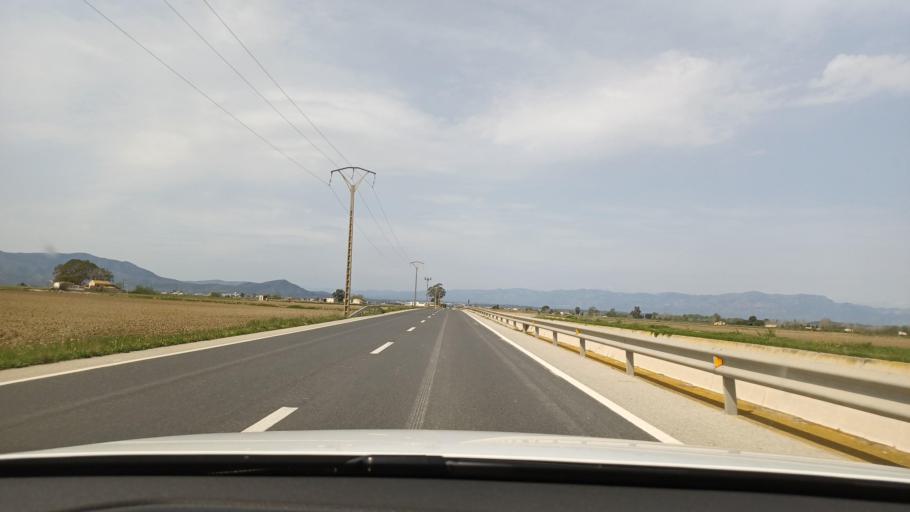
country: ES
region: Catalonia
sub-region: Provincia de Tarragona
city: Deltebre
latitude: 40.7107
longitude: 0.6681
